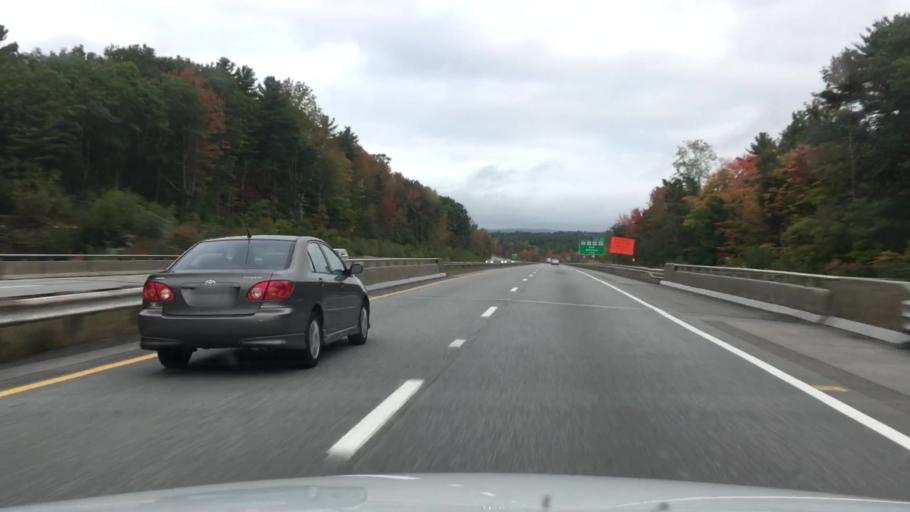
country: US
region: Maine
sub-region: Cumberland County
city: Cumberland Center
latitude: 43.8614
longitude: -70.3245
